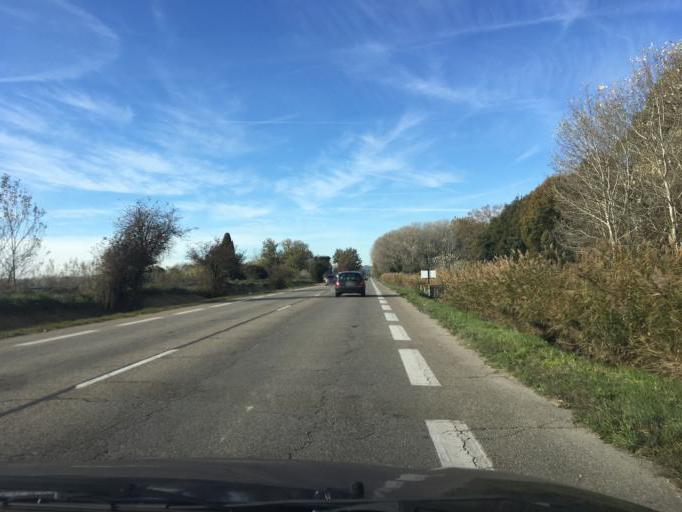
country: FR
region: Provence-Alpes-Cote d'Azur
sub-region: Departement du Vaucluse
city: Lauris
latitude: 43.7489
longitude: 5.2846
